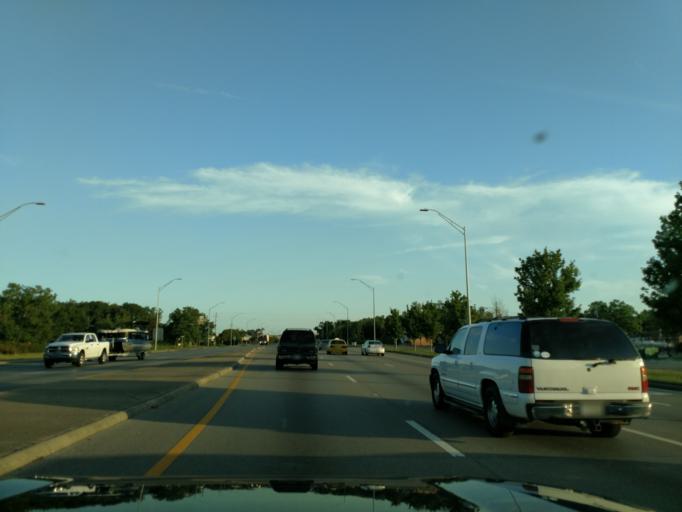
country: US
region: Mississippi
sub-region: Harrison County
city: West Gulfport
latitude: 30.4032
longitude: -89.0929
